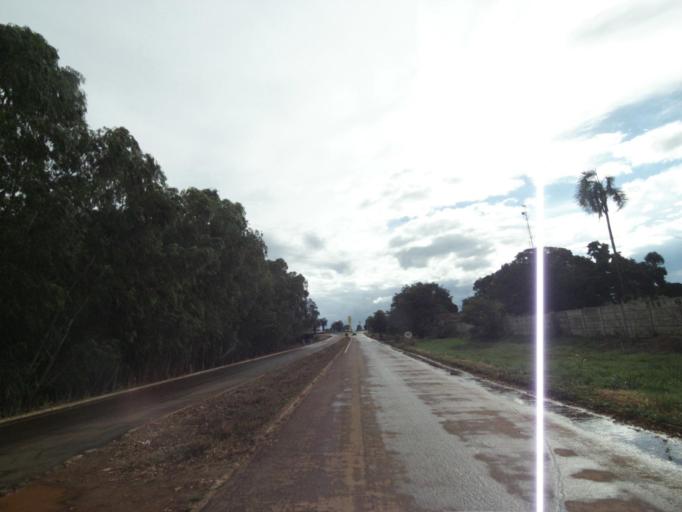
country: BR
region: Goias
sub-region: Itaberai
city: Itaberai
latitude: -15.9234
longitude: -49.6038
